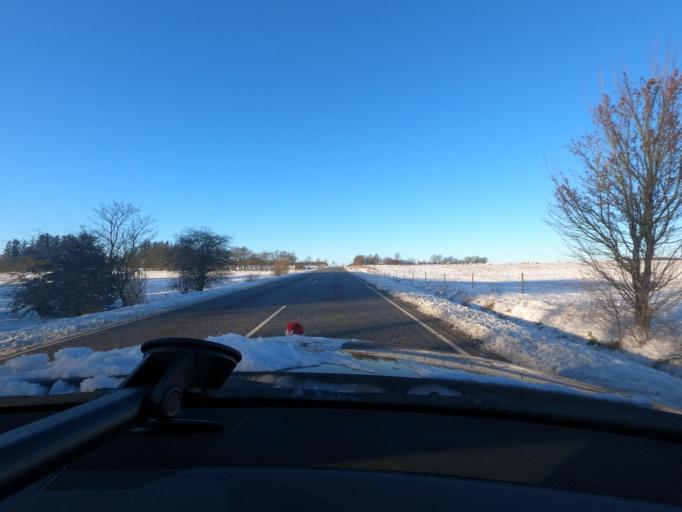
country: DK
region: South Denmark
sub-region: Tonder Kommune
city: Toftlund
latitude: 55.1186
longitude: 9.1587
